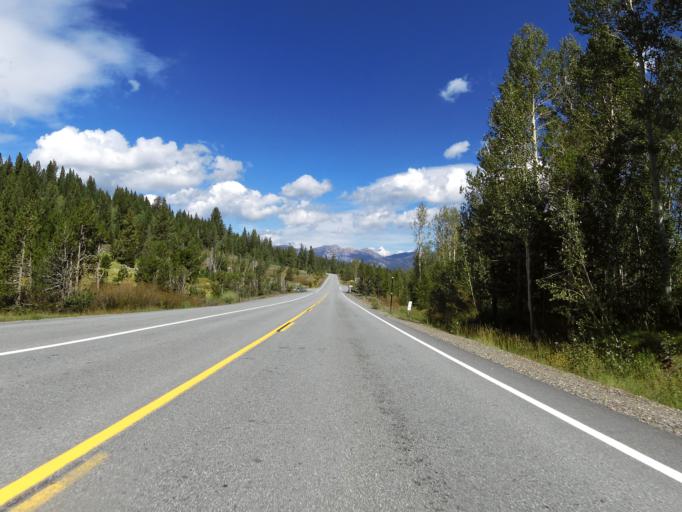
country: US
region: California
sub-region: El Dorado County
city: South Lake Tahoe
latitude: 38.7117
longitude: -119.9560
